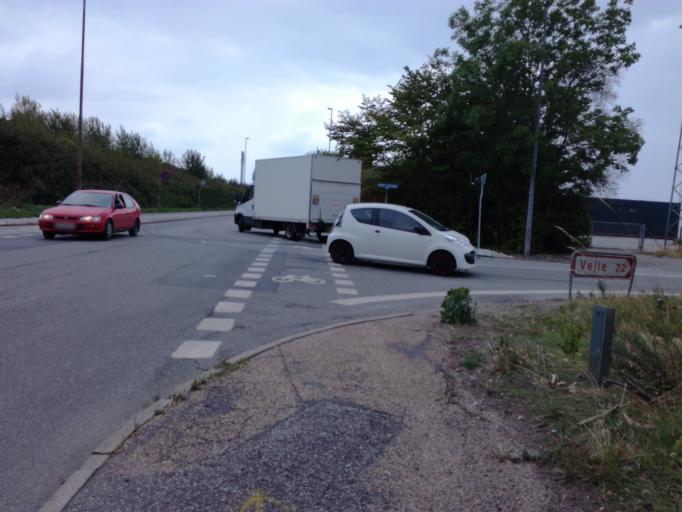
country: DK
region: South Denmark
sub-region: Fredericia Kommune
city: Fredericia
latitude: 55.5930
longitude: 9.7676
